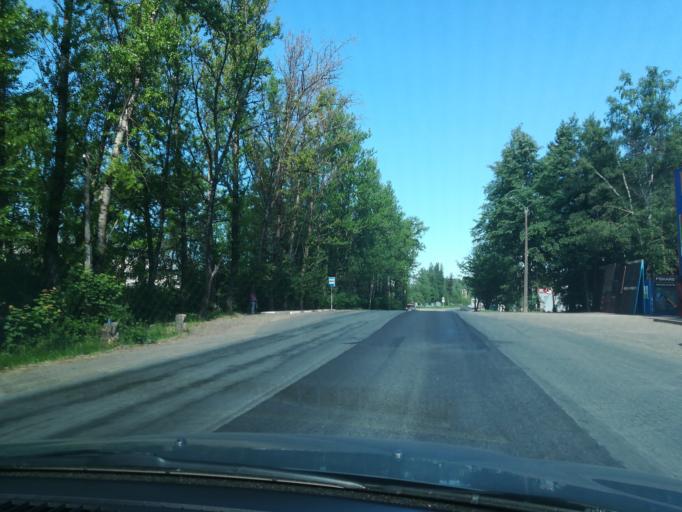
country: RU
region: Leningrad
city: Lesogorskiy
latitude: 61.0806
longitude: 28.9181
